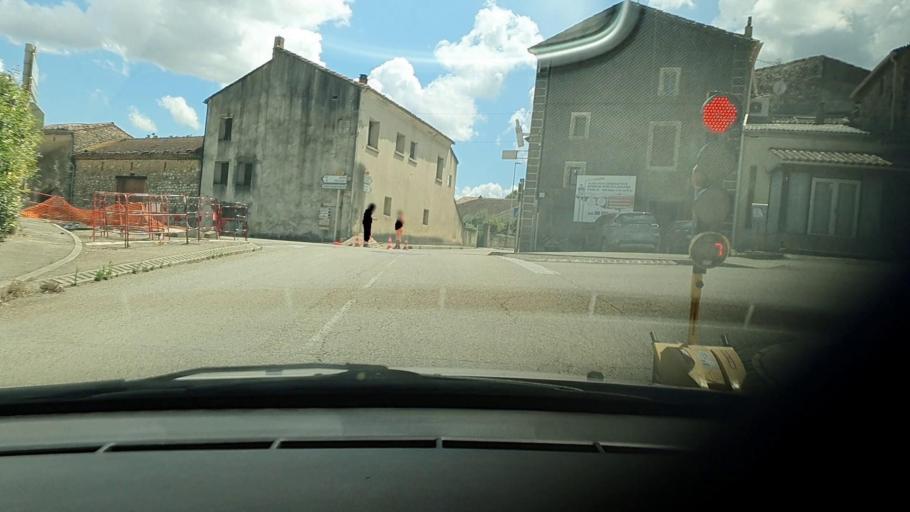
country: FR
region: Languedoc-Roussillon
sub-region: Departement du Gard
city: Moussac
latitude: 44.0322
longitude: 4.2333
